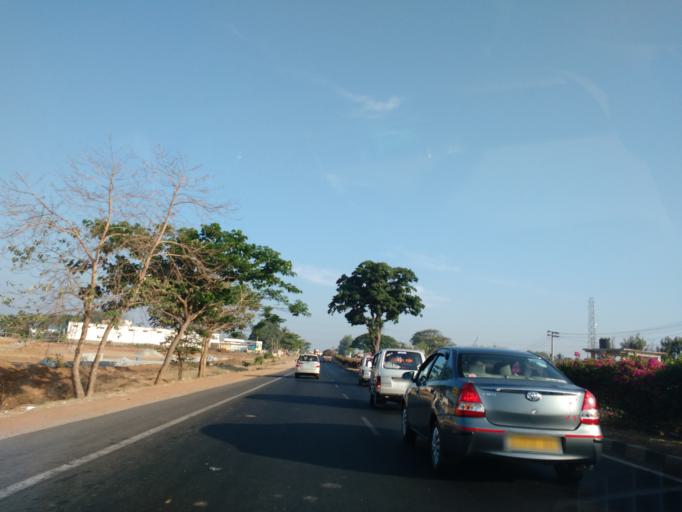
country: IN
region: Karnataka
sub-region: Bangalore Rural
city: Nelamangala
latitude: 13.1293
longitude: 77.3605
